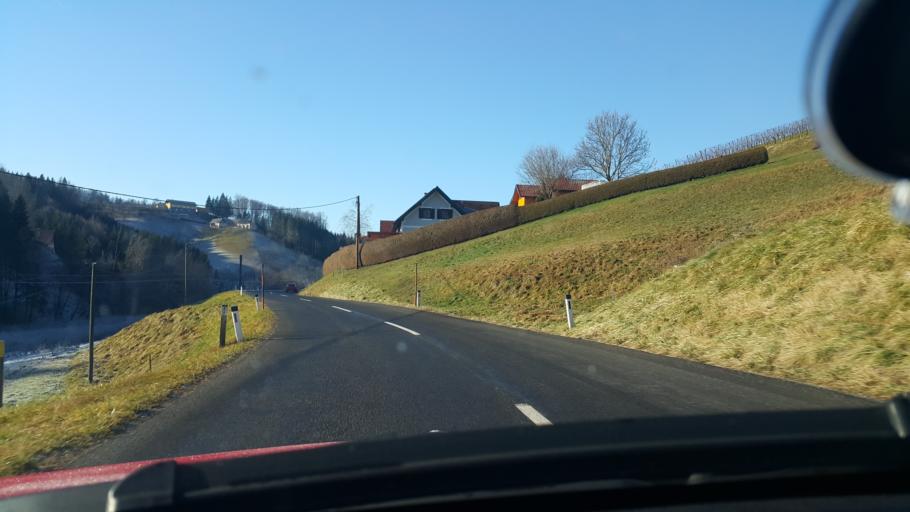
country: AT
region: Styria
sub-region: Politischer Bezirk Leibnitz
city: Leutschach
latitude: 46.6452
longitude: 15.5047
